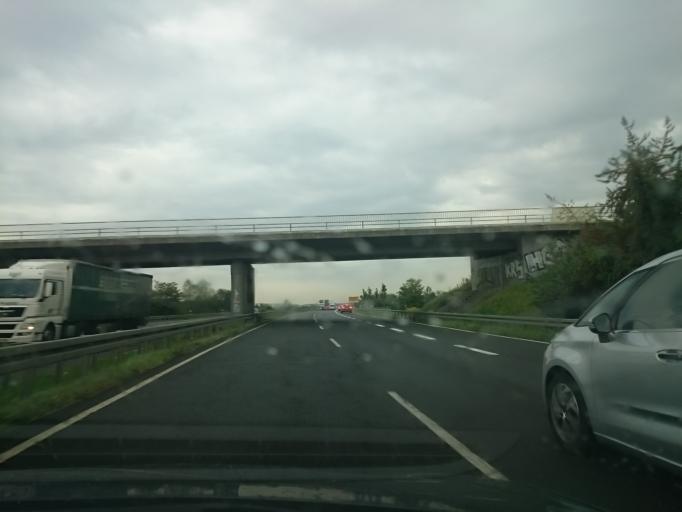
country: DE
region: Brandenburg
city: Leegebruch
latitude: 52.7398
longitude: 13.2068
